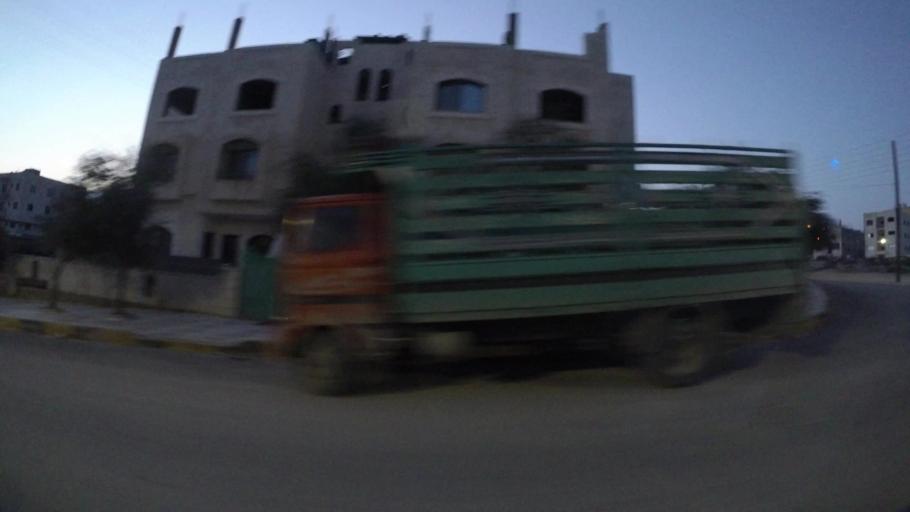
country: JO
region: Amman
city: Al Bunayyat ash Shamaliyah
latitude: 31.8885
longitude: 35.9244
